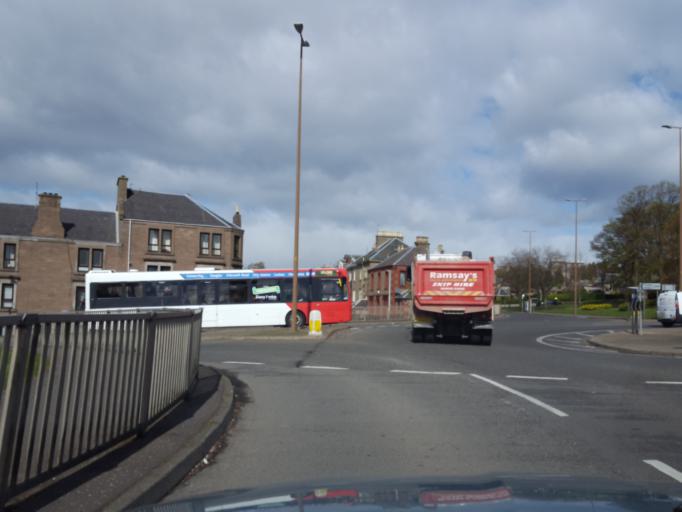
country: GB
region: Scotland
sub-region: Dundee City
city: Dundee
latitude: 56.4745
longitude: -3.0136
